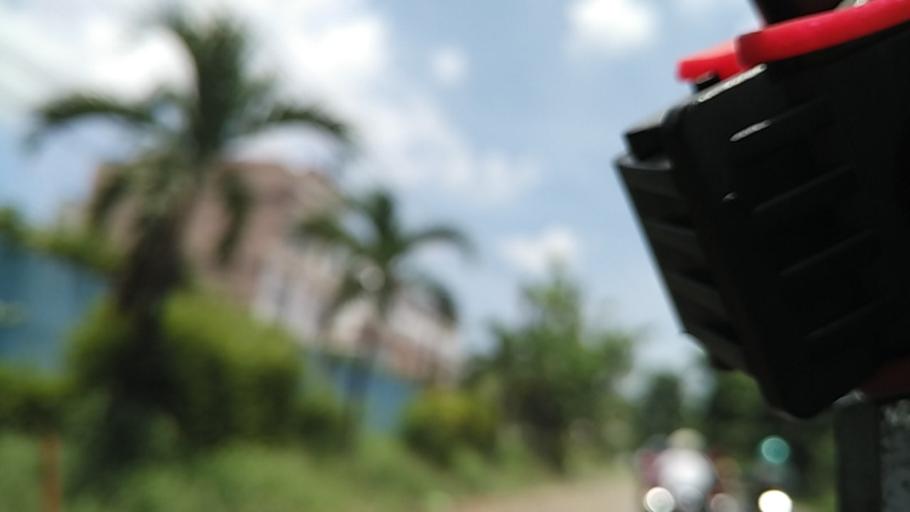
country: ID
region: Central Java
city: Semarang
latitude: -7.0073
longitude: 110.3880
